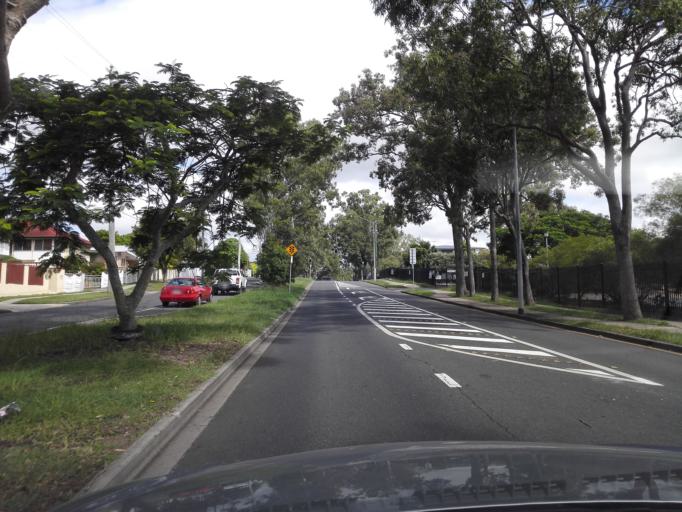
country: AU
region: Queensland
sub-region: Brisbane
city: Zillmere
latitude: -27.3574
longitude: 153.0249
